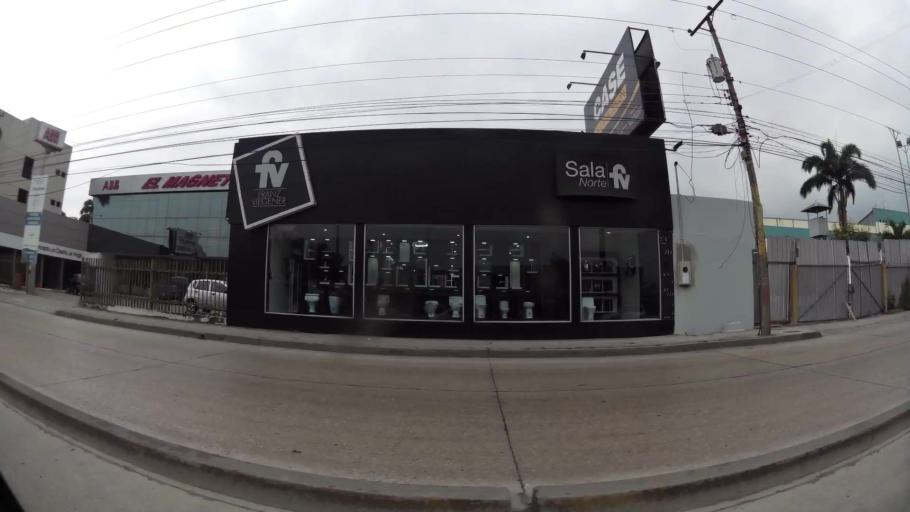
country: EC
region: Guayas
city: Eloy Alfaro
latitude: -2.1500
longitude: -79.8998
